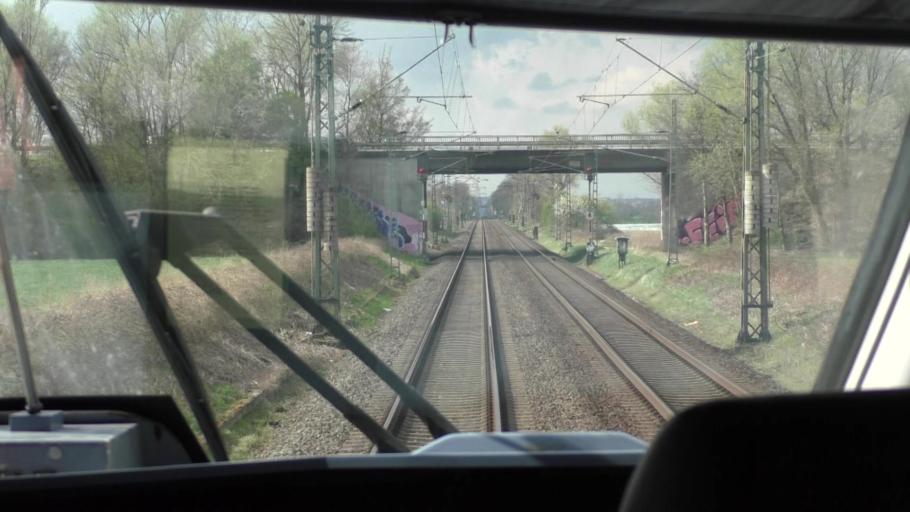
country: DE
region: North Rhine-Westphalia
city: Bornheim
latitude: 50.7738
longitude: 6.9889
